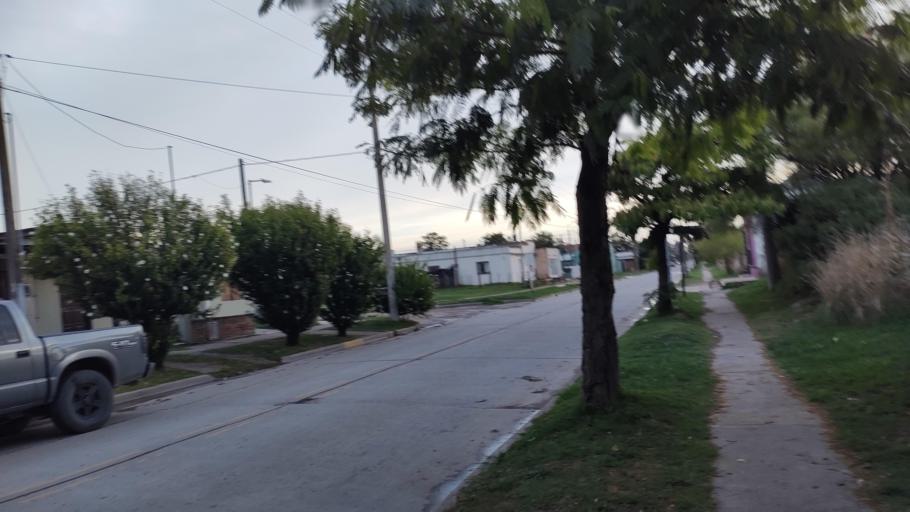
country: AR
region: Buenos Aires
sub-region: Partido de Loberia
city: Loberia
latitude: -38.1751
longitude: -58.7753
